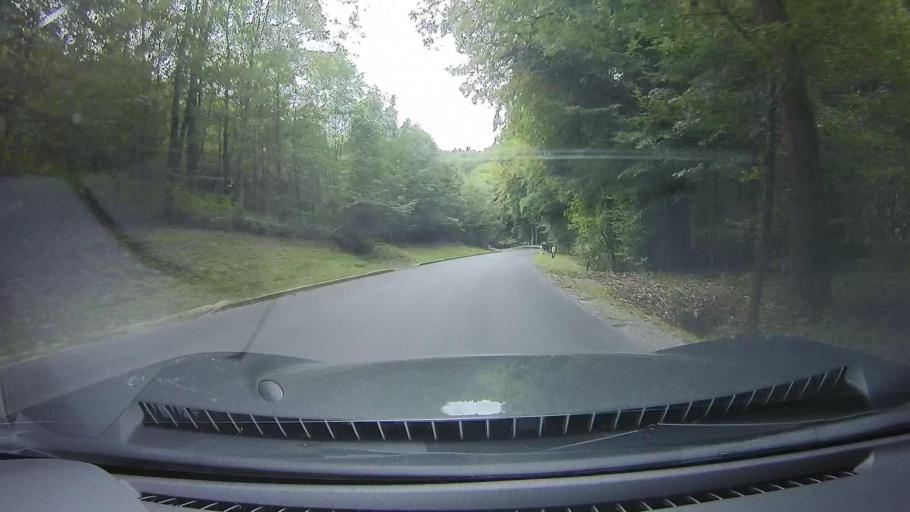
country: DE
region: Baden-Wuerttemberg
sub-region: Regierungsbezirk Stuttgart
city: Althutte
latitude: 48.9103
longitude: 9.5479
